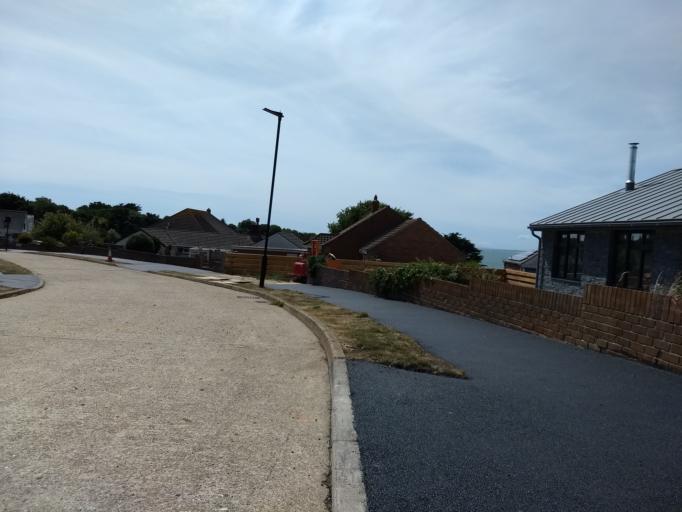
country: GB
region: England
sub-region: Isle of Wight
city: Gurnard
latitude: 50.7611
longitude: -1.3204
